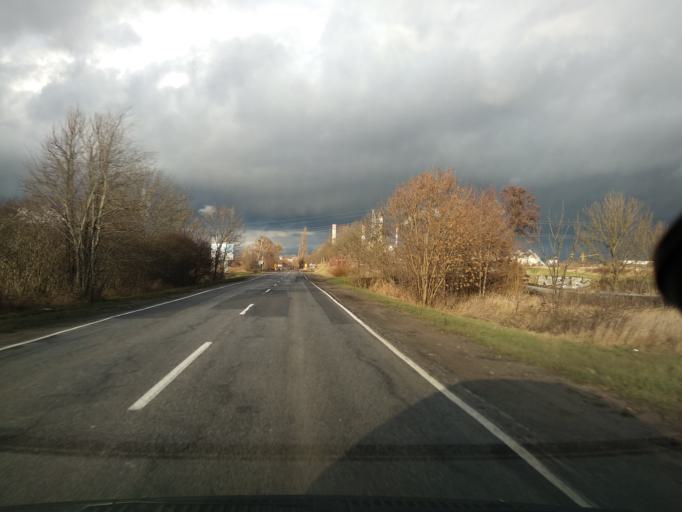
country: PL
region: Greater Poland Voivodeship
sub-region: Konin
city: Konin
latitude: 52.2731
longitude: 18.2669
